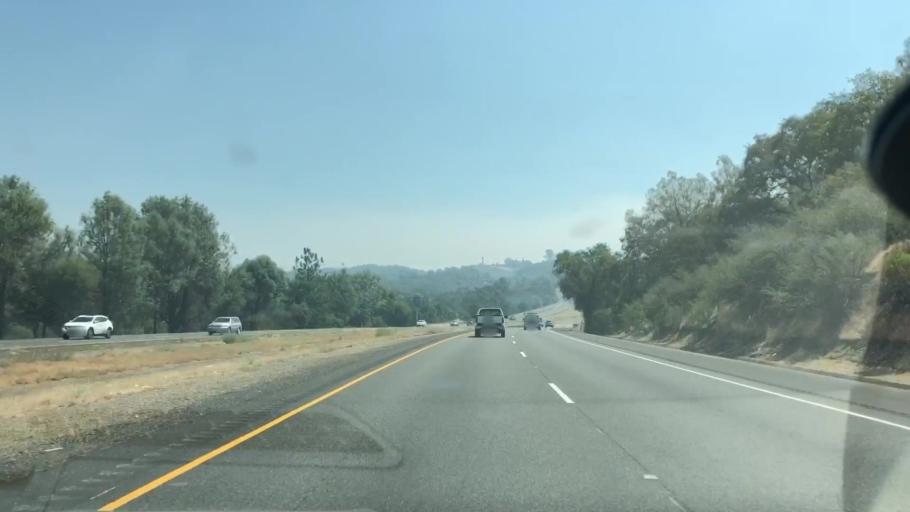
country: US
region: California
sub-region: El Dorado County
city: Shingle Springs
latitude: 38.6954
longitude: -120.8907
